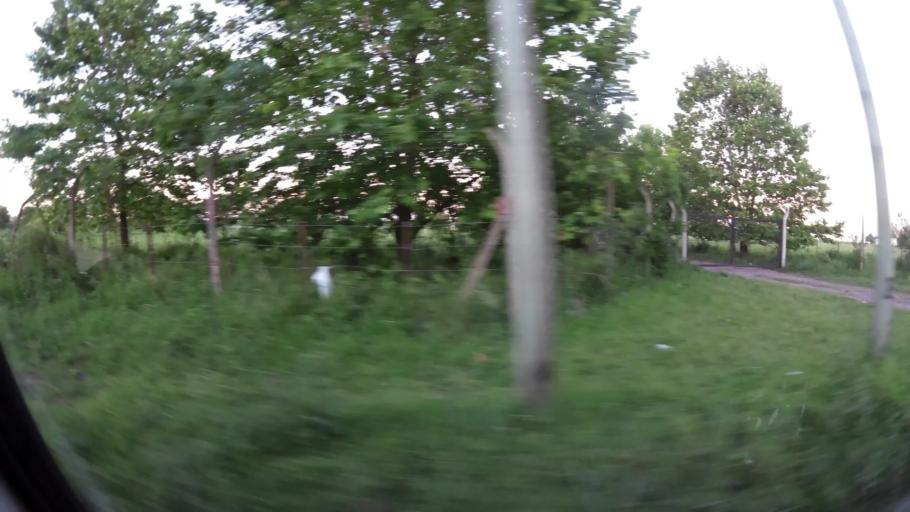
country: AR
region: Buenos Aires
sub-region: Partido de Quilmes
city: Quilmes
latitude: -34.8008
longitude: -58.1852
